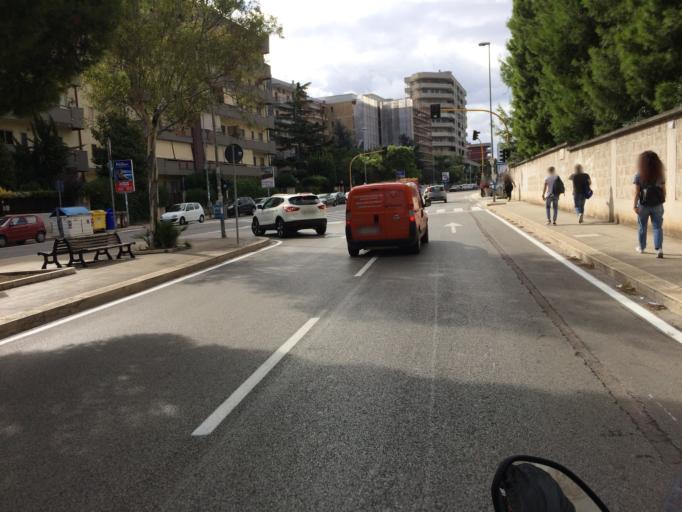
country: IT
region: Apulia
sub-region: Provincia di Bari
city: Bari
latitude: 41.0952
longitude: 16.8545
